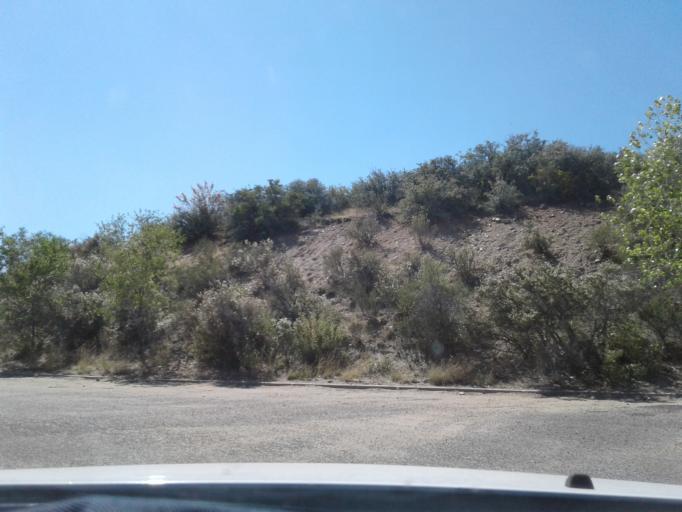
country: US
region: Arizona
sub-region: Yavapai County
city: Prescott
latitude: 34.5492
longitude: -112.4449
